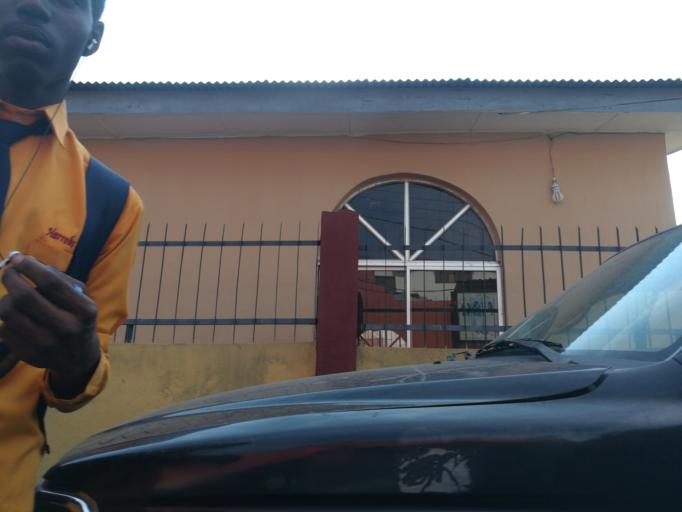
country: NG
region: Lagos
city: Ojota
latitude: 6.5938
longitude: 3.4000
